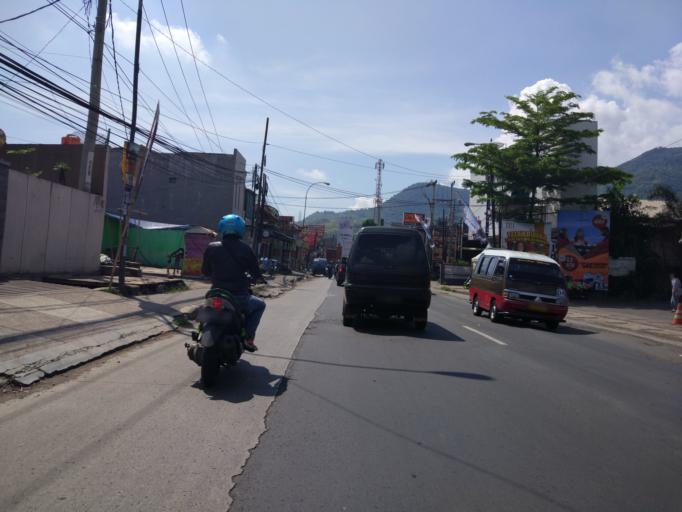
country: ID
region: West Java
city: Cileunyi
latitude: -6.9317
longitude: 107.7787
